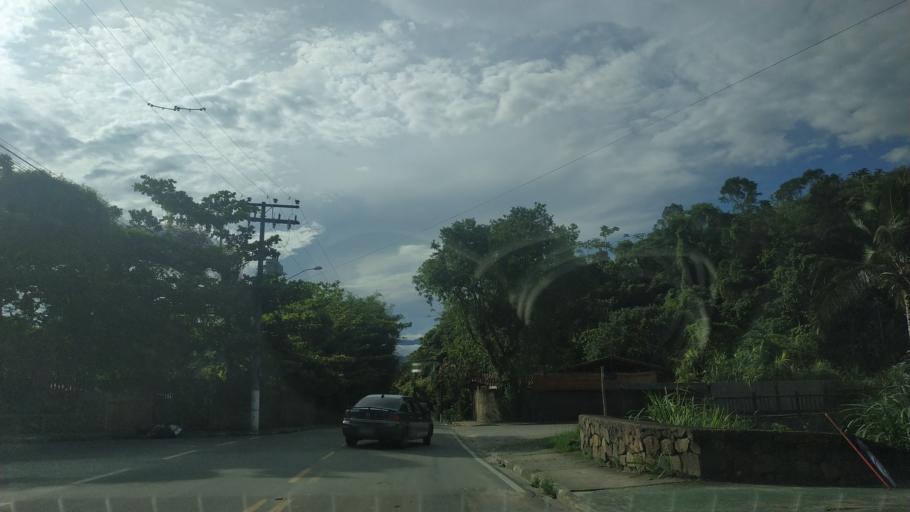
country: BR
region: Sao Paulo
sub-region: Ilhabela
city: Ilhabela
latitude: -23.8282
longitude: -45.3573
